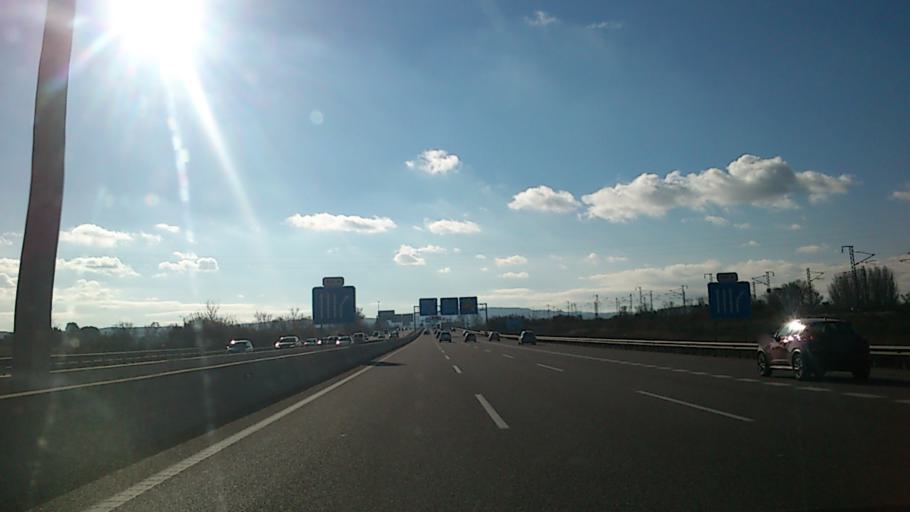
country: ES
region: Aragon
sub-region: Provincia de Zaragoza
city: Oliver-Valdefierro, Oliver, Valdefierro
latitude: 41.6521
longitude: -0.9598
